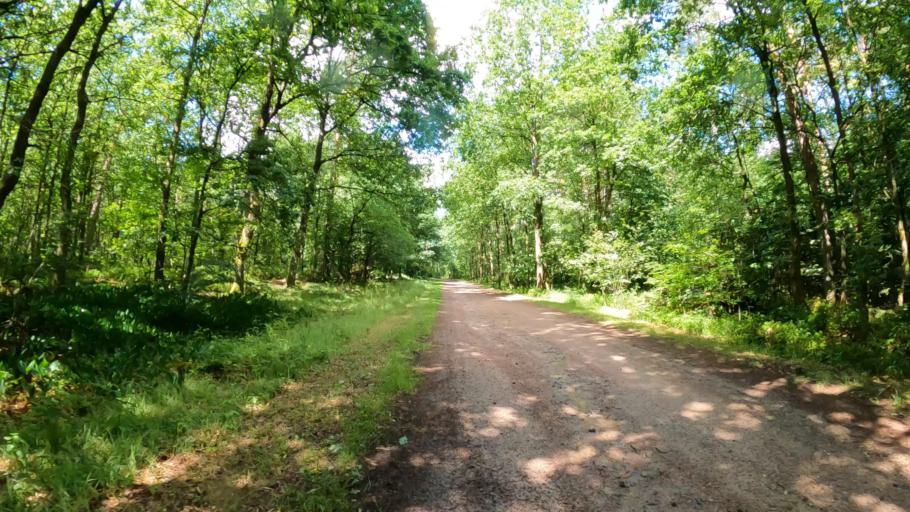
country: DE
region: Lower Saxony
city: Neu Wulmstorf
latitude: 53.4139
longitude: 9.8129
